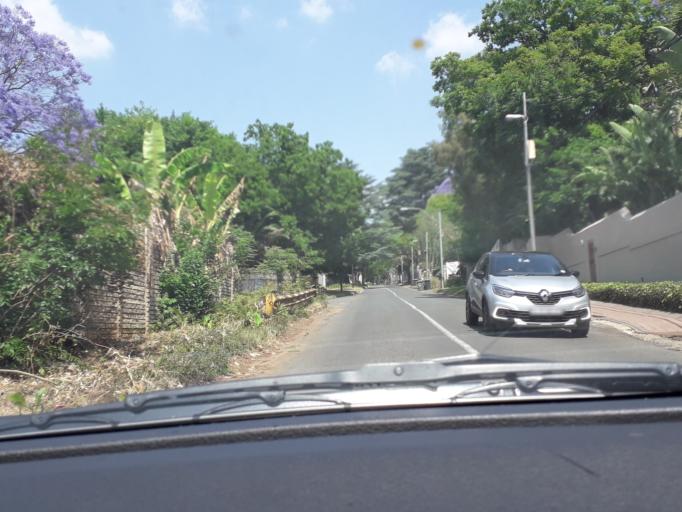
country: ZA
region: Gauteng
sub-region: City of Johannesburg Metropolitan Municipality
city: Johannesburg
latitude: -26.1230
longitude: 28.0698
